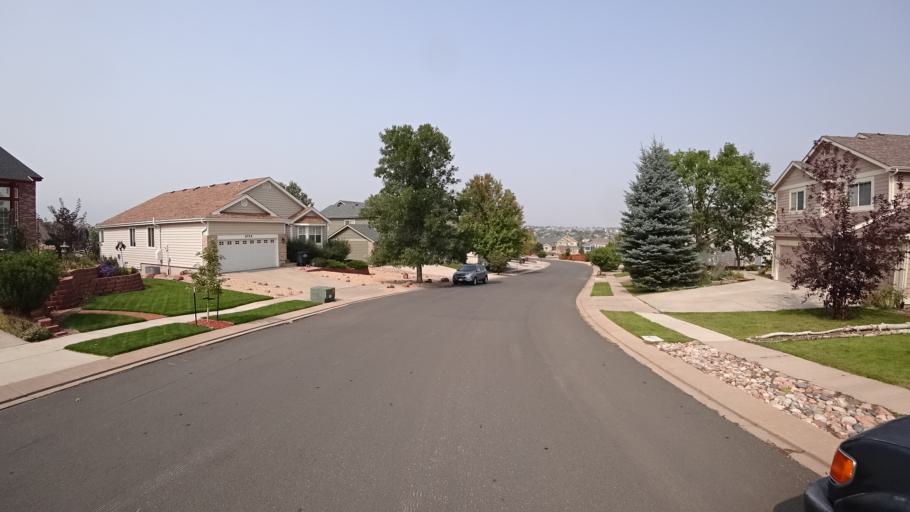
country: US
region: Colorado
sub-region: El Paso County
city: Cimarron Hills
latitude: 38.9261
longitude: -104.7466
